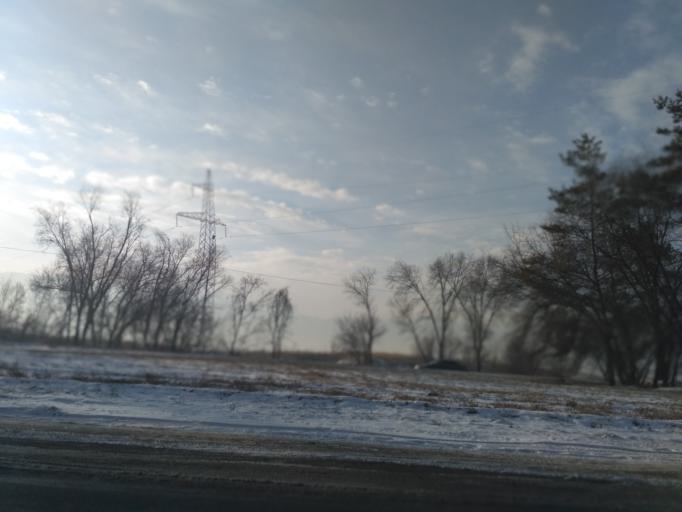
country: KZ
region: Almaty Oblysy
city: Burunday
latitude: 43.2140
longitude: 76.6789
